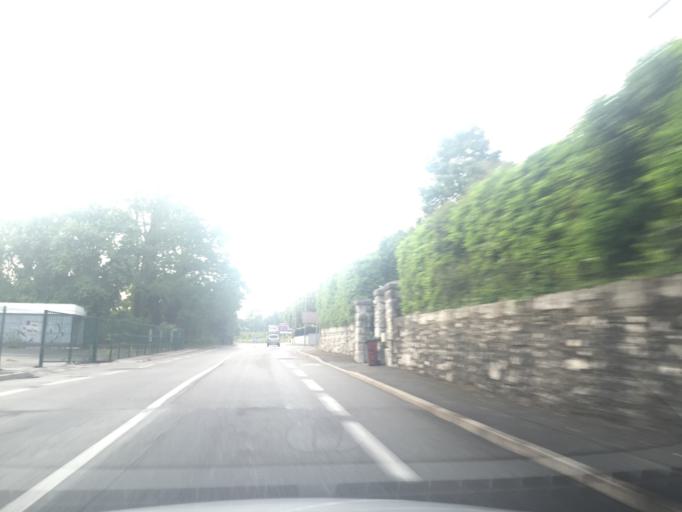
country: FR
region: Rhone-Alpes
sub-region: Departement de la Savoie
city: Chambery
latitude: 45.5820
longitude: 5.9245
